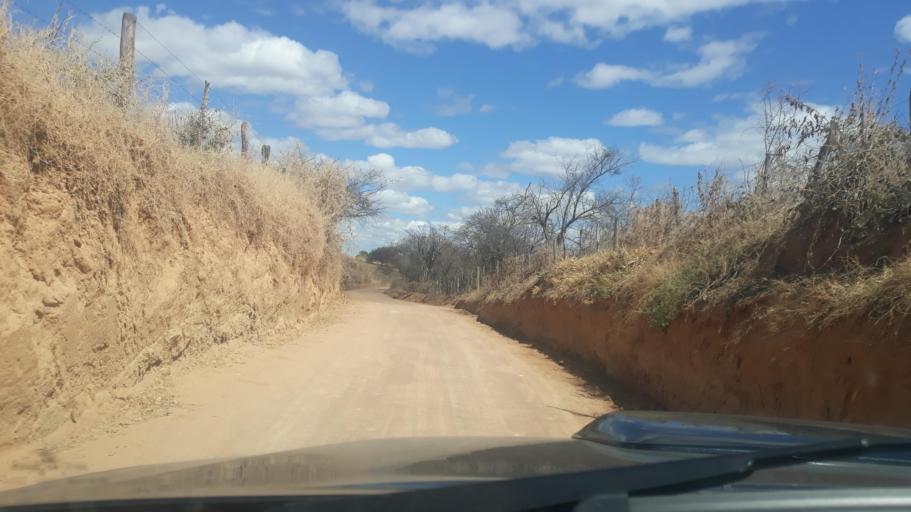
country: BR
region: Bahia
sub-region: Riacho De Santana
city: Riacho de Santana
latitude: -13.8974
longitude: -42.8504
